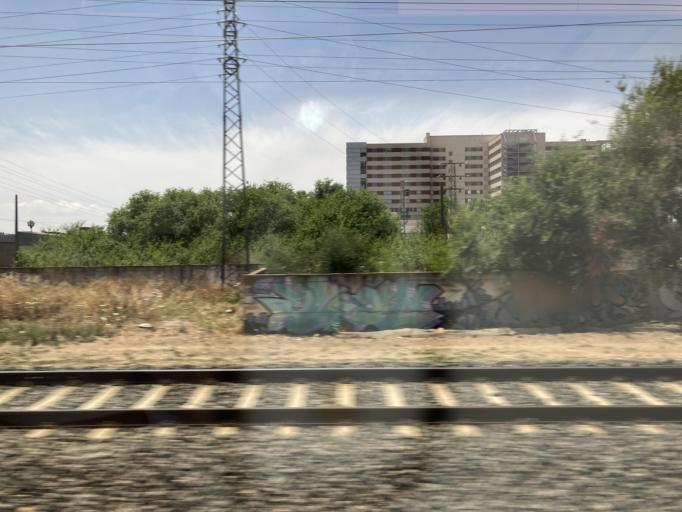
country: ES
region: Andalusia
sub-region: Provincia de Sevilla
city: Sevilla
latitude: 37.3463
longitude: -5.9690
